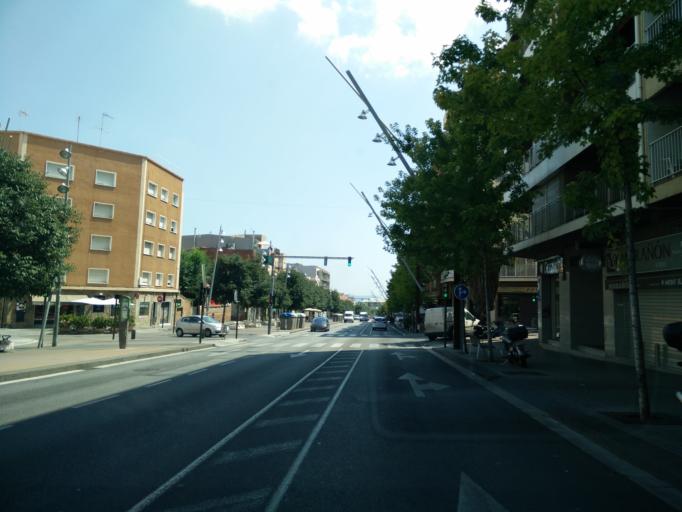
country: ES
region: Catalonia
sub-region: Provincia de Barcelona
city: Terrassa
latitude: 41.5639
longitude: 2.0272
